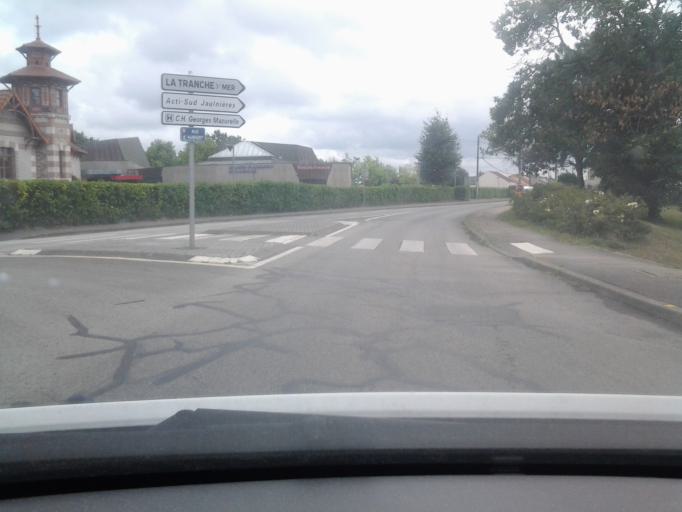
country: FR
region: Pays de la Loire
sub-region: Departement de la Vendee
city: La Roche-sur-Yon
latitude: 46.6579
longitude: -1.4318
